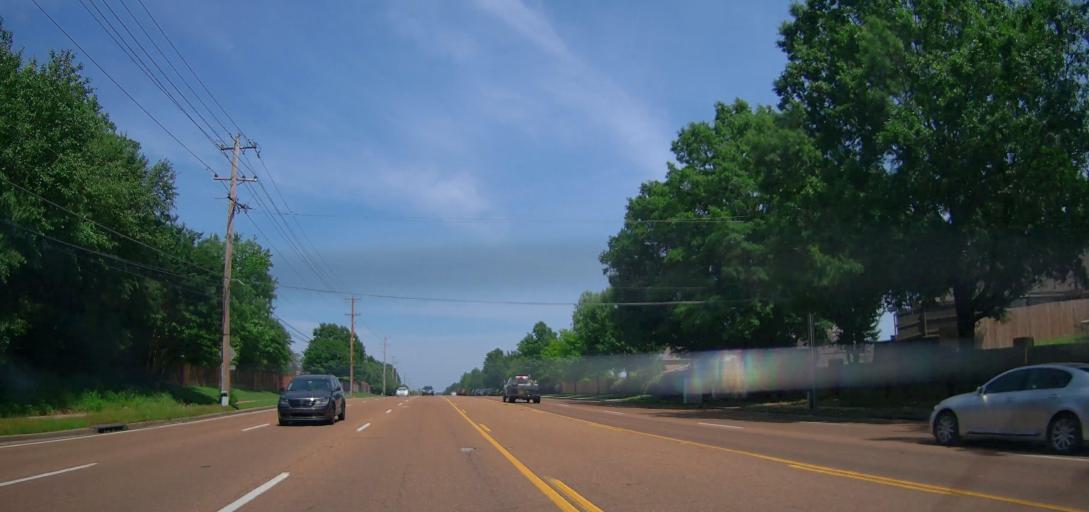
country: US
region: Mississippi
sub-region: De Soto County
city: Olive Branch
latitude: 35.0205
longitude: -89.8159
